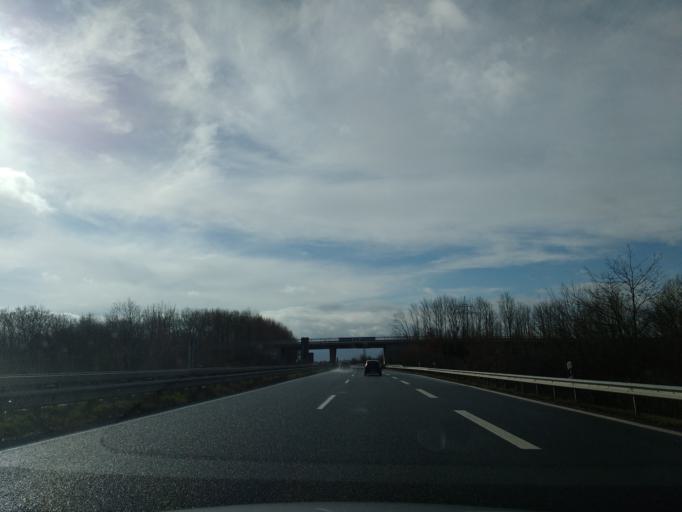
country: DE
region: Lower Saxony
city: Cuxhaven
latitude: 53.8154
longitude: 8.7084
